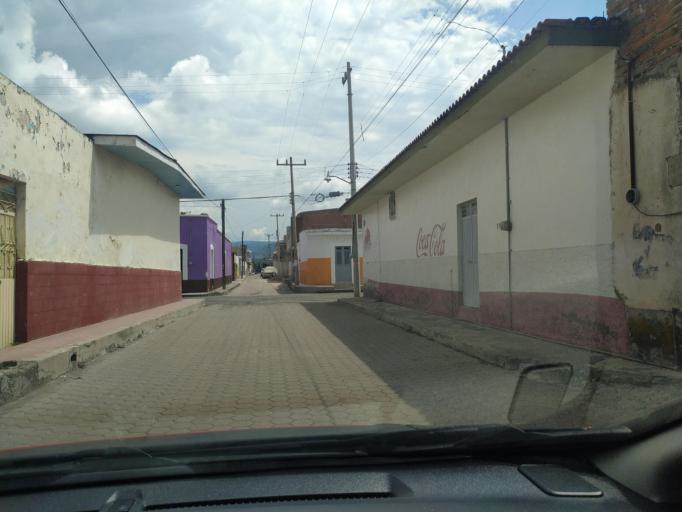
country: MX
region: Jalisco
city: Villa Corona
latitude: 20.3498
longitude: -103.6721
